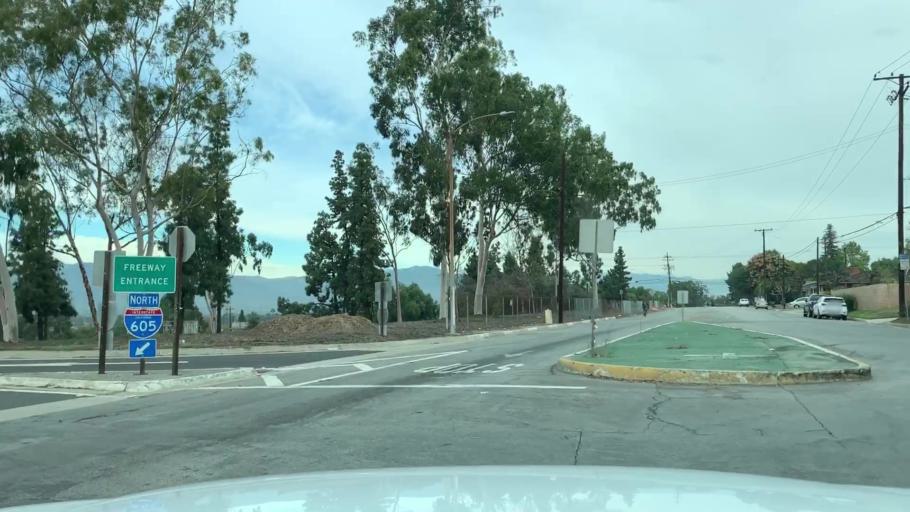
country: US
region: California
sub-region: Los Angeles County
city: West Whittier-Los Nietos
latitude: 34.0049
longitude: -118.0618
